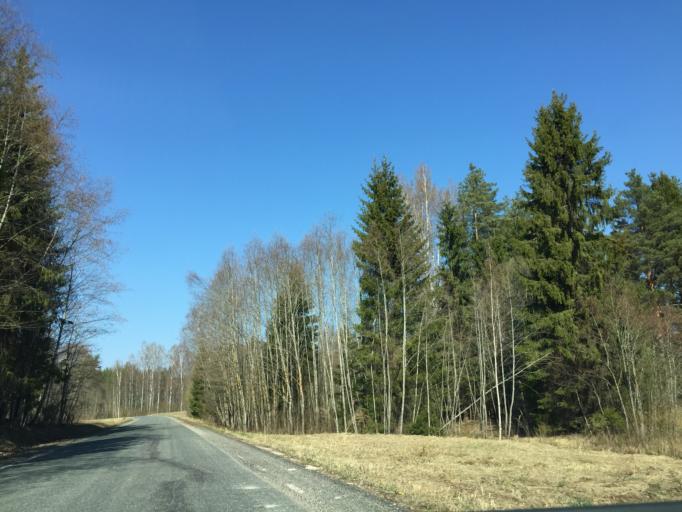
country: EE
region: Tartu
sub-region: Alatskivi vald
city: Kallaste
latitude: 58.5803
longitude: 26.9082
